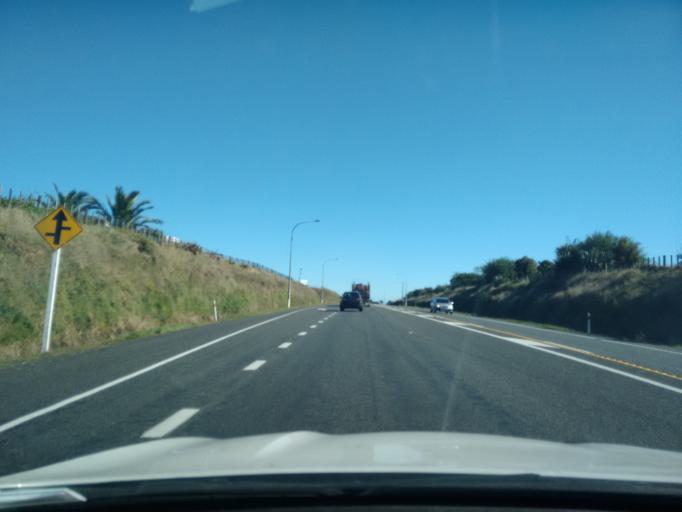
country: NZ
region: Taranaki
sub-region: New Plymouth District
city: New Plymouth
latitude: -39.1367
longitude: 174.1294
